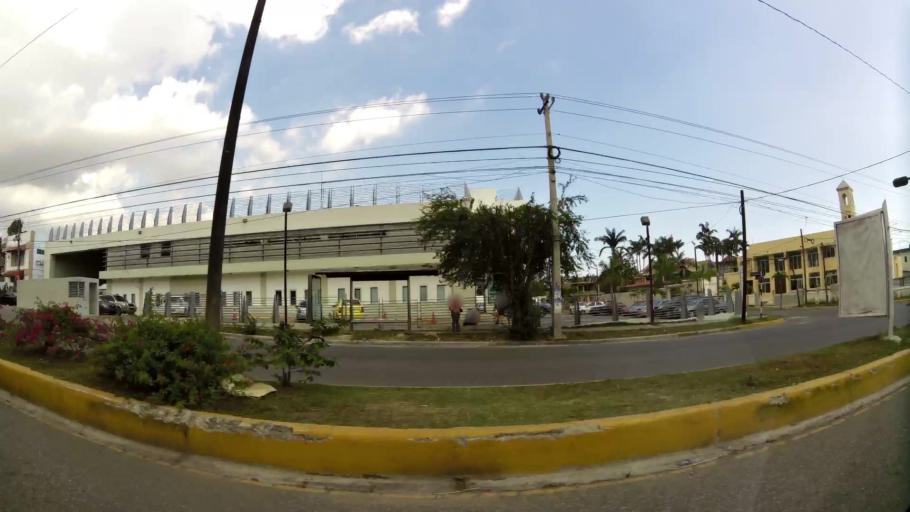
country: DO
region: Santo Domingo
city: Santo Domingo Oeste
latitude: 18.4924
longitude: -70.0000
